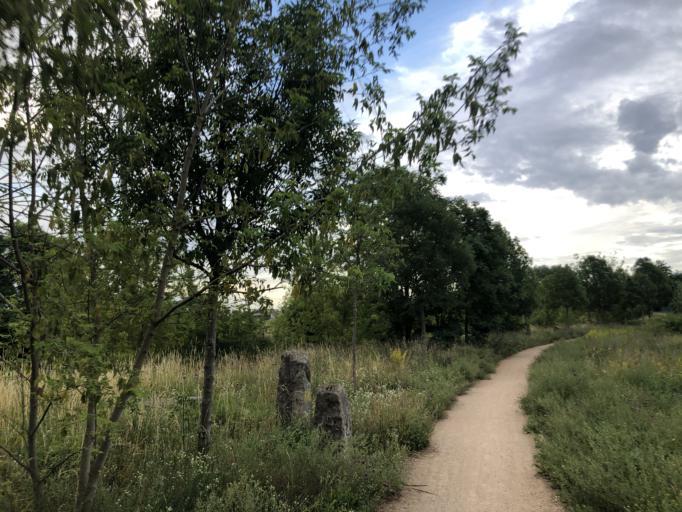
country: DE
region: Berlin
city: Falkenberg
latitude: 52.5493
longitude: 13.5315
